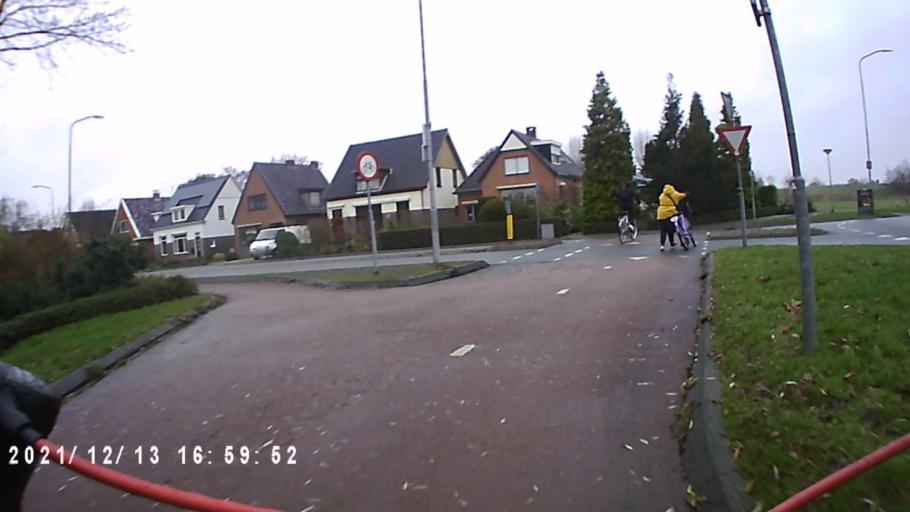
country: NL
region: Groningen
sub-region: Gemeente Appingedam
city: Appingedam
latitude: 53.3195
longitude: 6.8784
